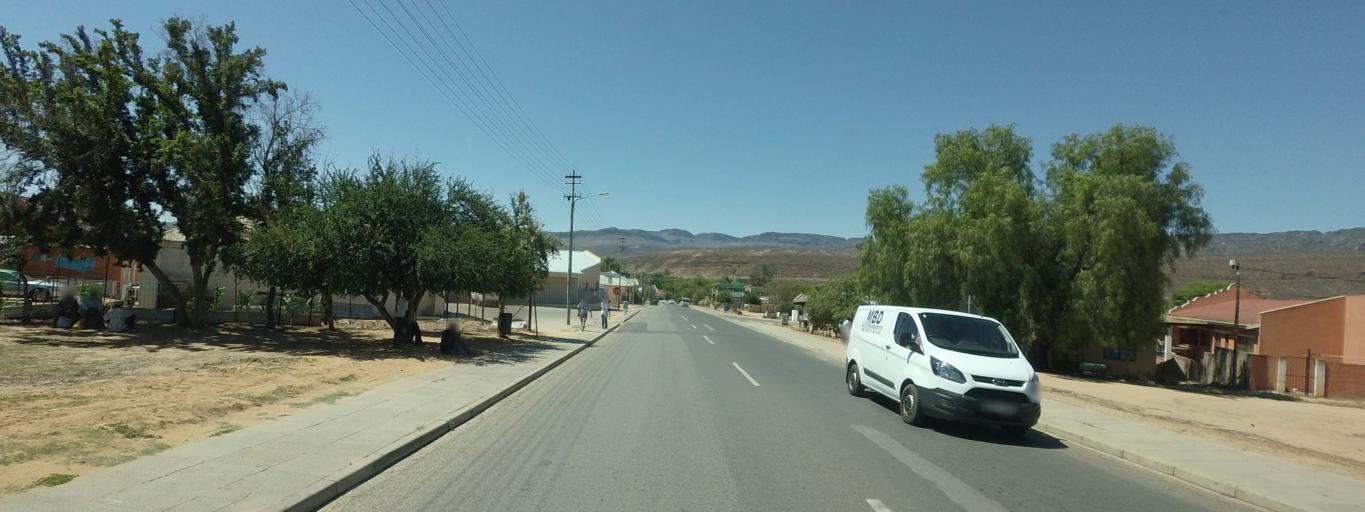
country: ZA
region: Western Cape
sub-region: West Coast District Municipality
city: Clanwilliam
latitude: -32.1834
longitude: 18.8924
